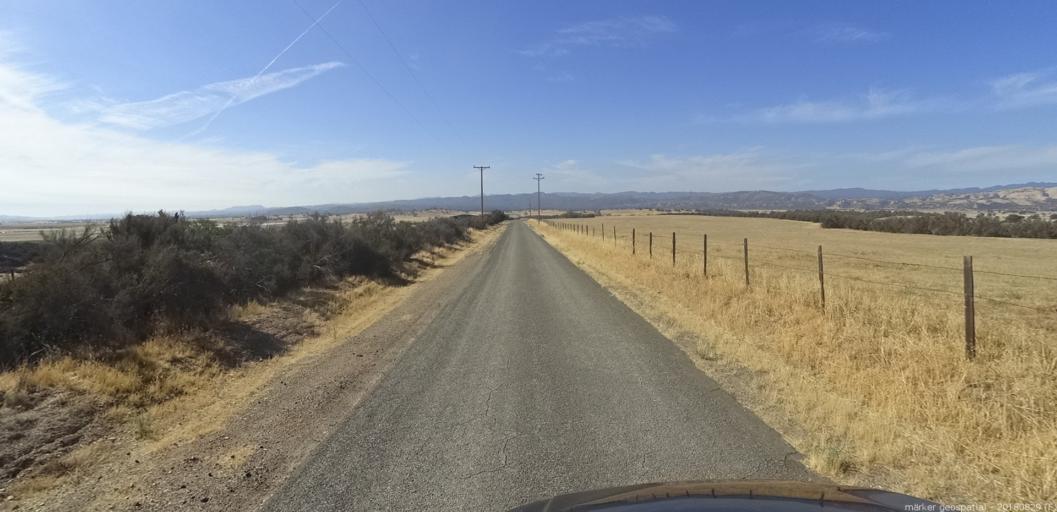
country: US
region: California
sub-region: Monterey County
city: King City
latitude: 35.9792
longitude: -121.1174
